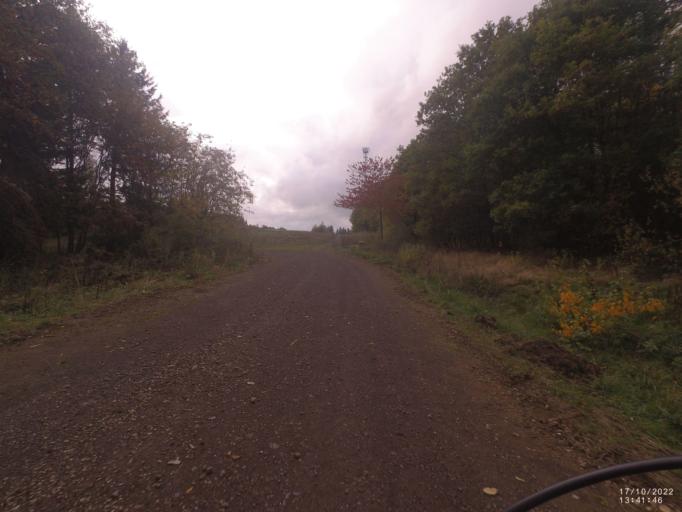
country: DE
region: Rheinland-Pfalz
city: Horscheid
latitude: 50.2222
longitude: 6.8627
